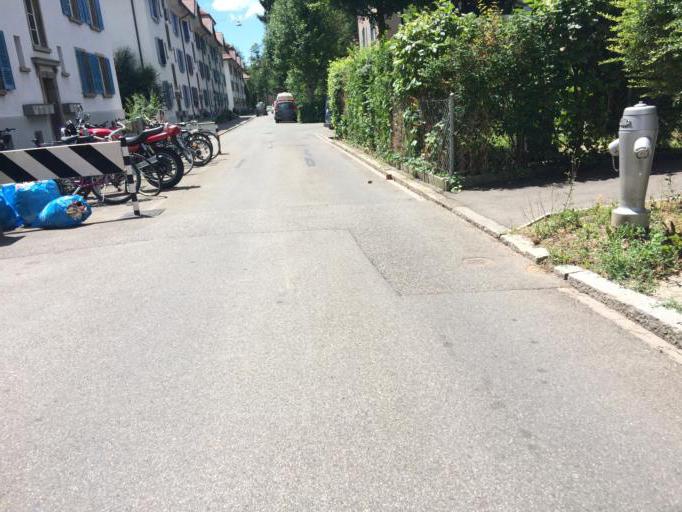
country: CH
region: Bern
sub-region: Bern-Mittelland District
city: Muri
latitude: 46.9418
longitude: 7.4701
